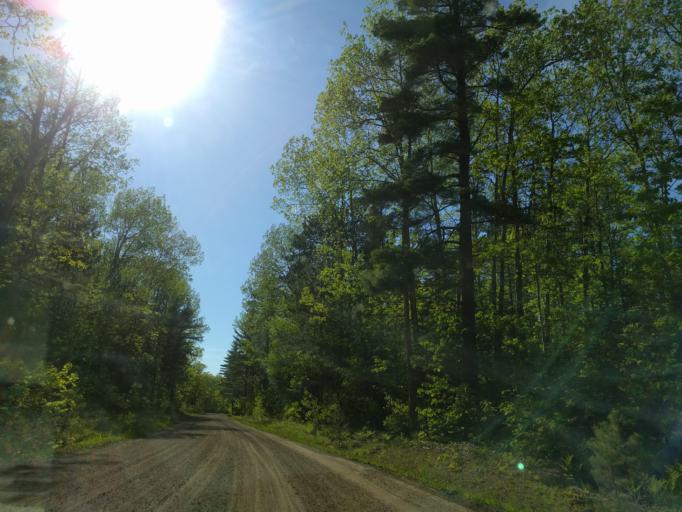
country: US
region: Michigan
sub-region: Marquette County
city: Gwinn
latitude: 46.2692
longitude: -87.3612
